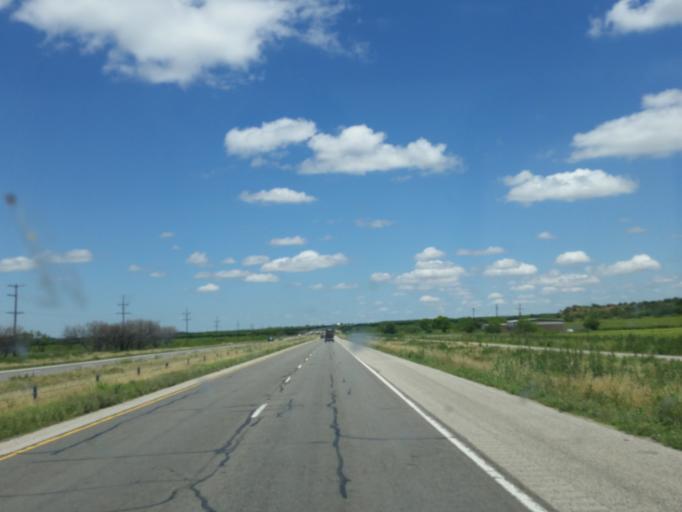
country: US
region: Texas
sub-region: Nolan County
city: Sweetwater
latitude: 32.4945
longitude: -100.2901
